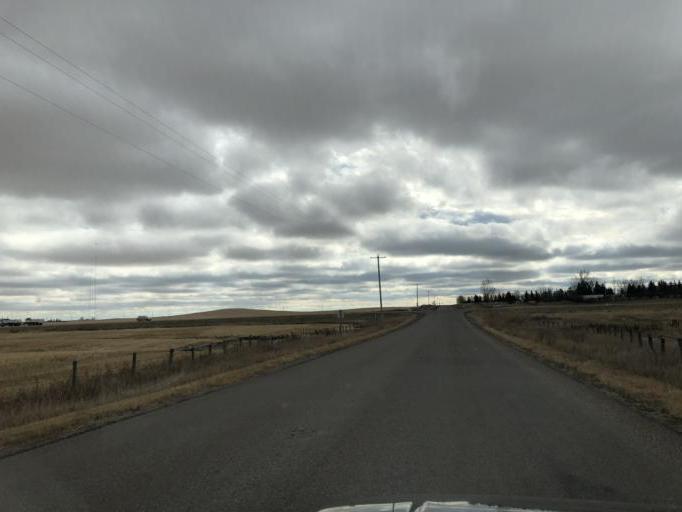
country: CA
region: Alberta
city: Chestermere
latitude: 50.9088
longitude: -113.8830
